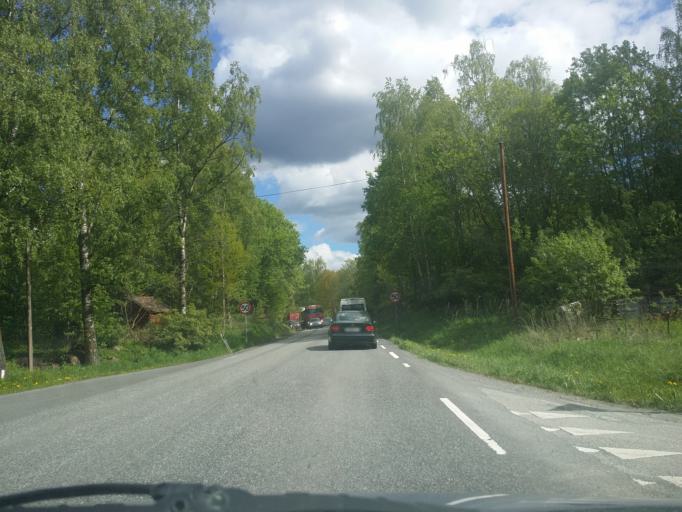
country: NO
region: Oppland
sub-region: Jevnaker
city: Jevnaker
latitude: 60.2668
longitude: 10.4838
